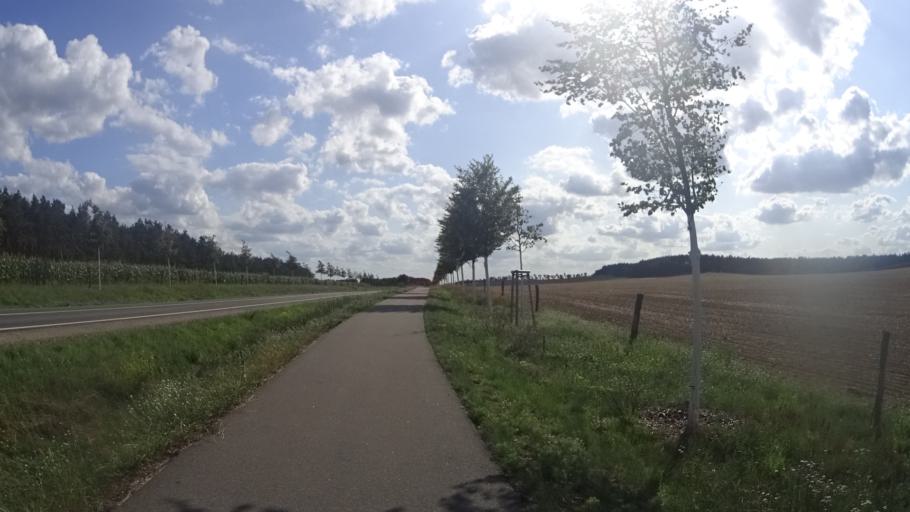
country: DE
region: Brandenburg
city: Rhinow
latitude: 52.7011
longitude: 12.3704
